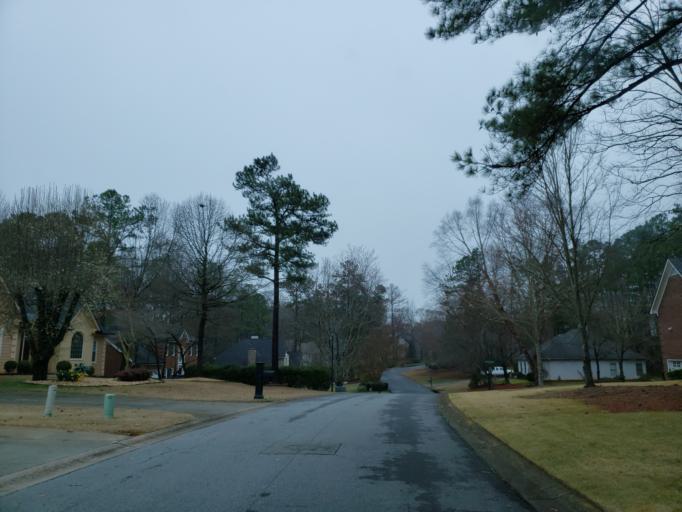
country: US
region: Georgia
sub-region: Cobb County
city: Fair Oaks
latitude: 33.9289
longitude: -84.5786
